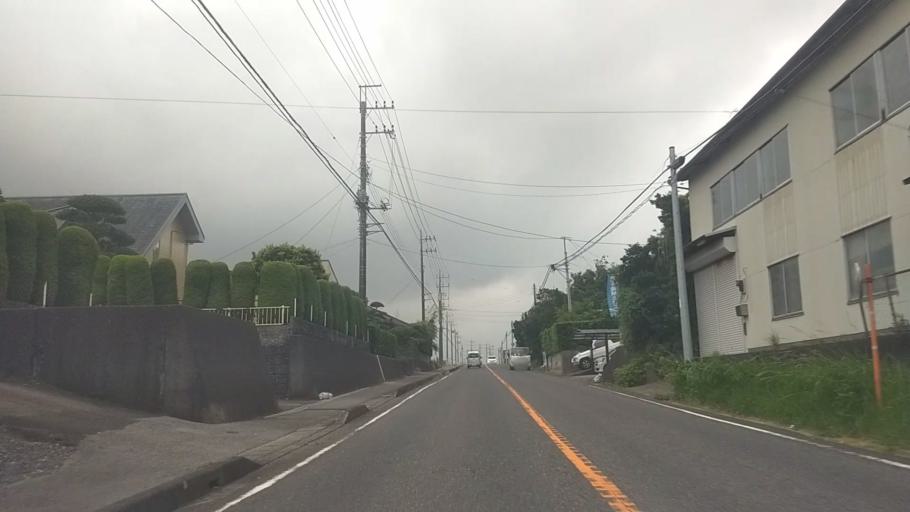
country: JP
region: Chiba
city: Kawaguchi
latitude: 35.1296
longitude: 140.0305
